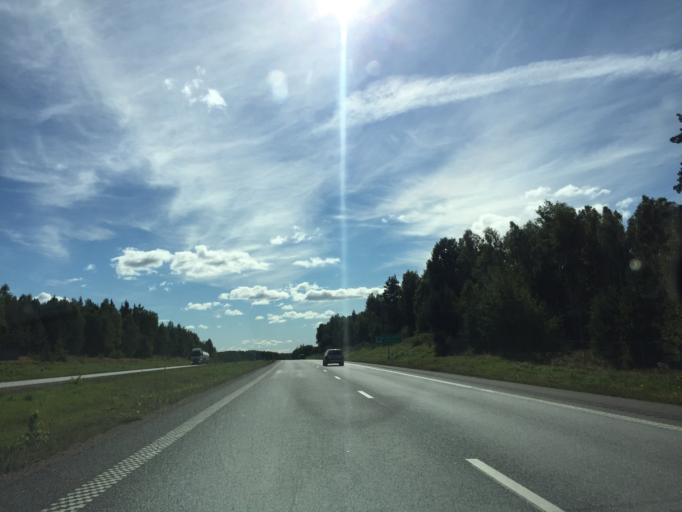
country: SE
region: Vaestmanland
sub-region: Arboga Kommun
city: Arboga
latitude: 59.4660
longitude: 15.8994
